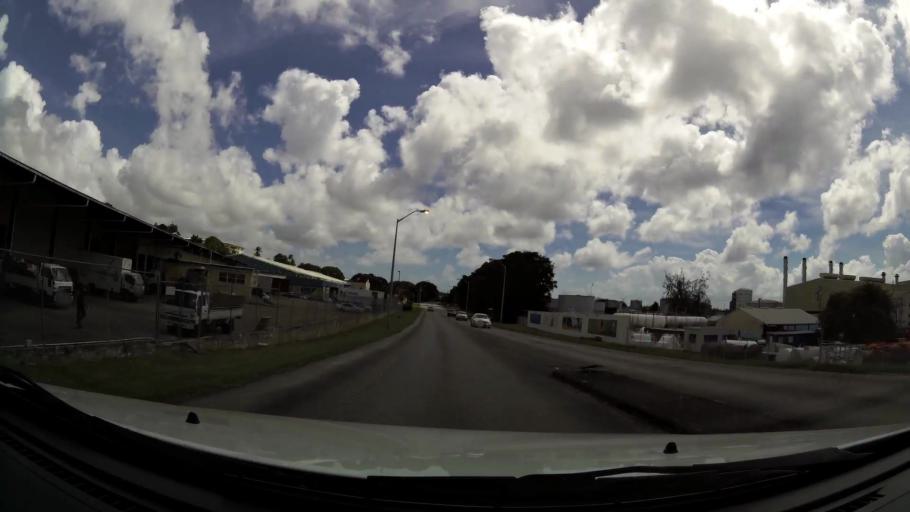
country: BB
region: Saint Michael
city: Bridgetown
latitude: 13.1273
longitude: -59.6317
